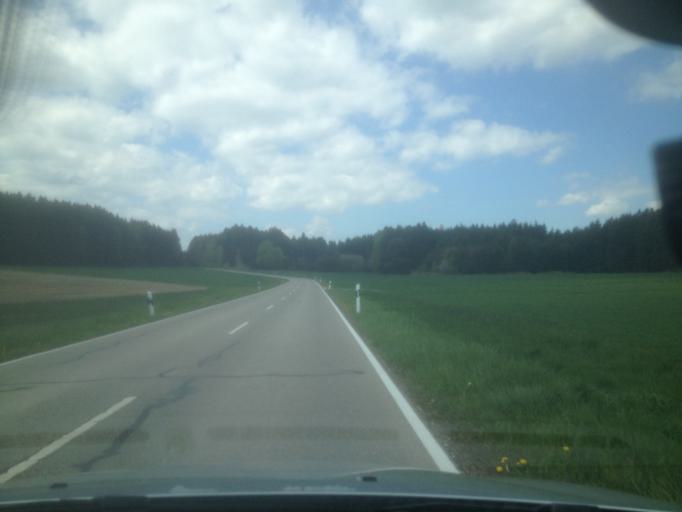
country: DE
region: Bavaria
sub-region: Swabia
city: Landensberg
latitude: 48.4595
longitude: 10.5398
